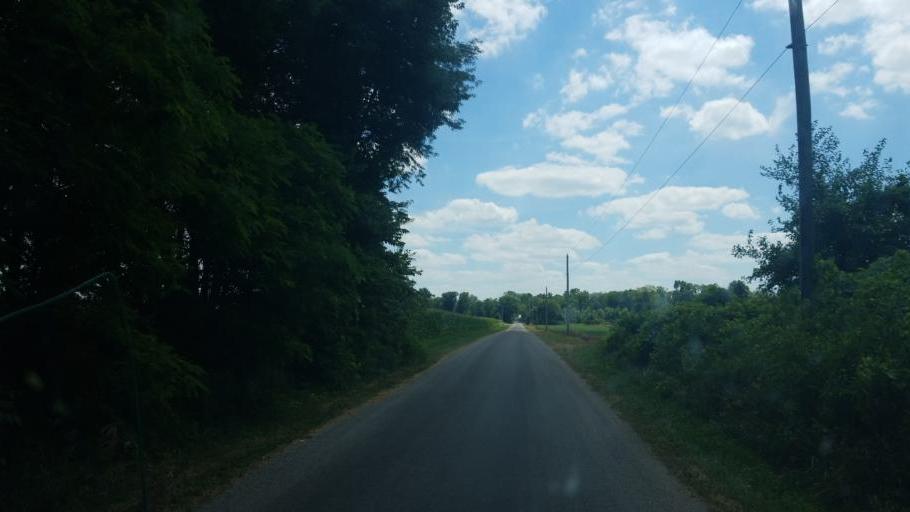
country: US
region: Ohio
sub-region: Williams County
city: Edgerton
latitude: 41.3680
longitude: -84.6903
